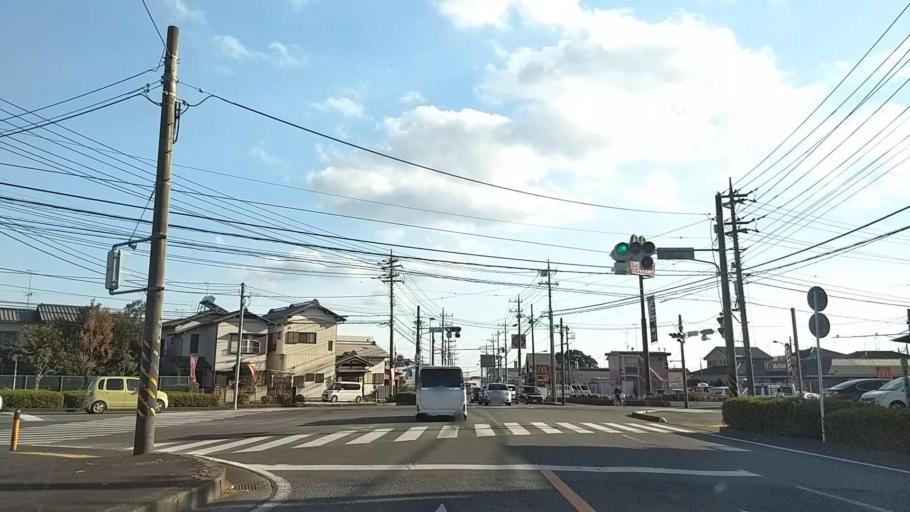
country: JP
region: Kanagawa
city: Atsugi
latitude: 35.4535
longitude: 139.3294
